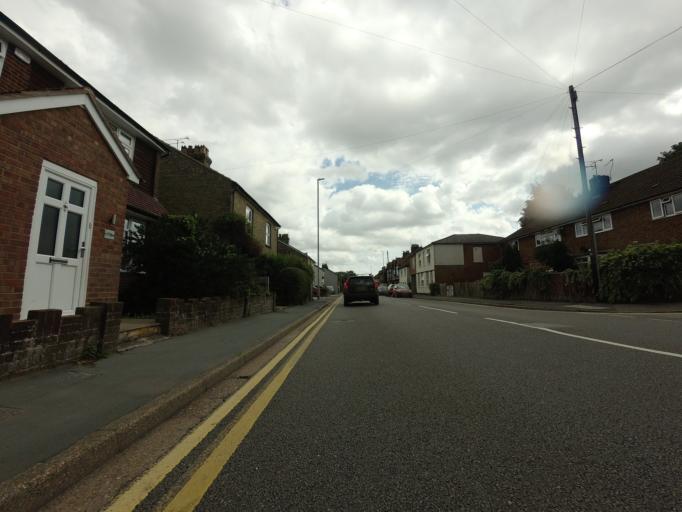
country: GB
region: England
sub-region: Kent
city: Sevenoaks
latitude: 51.2968
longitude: 0.1648
